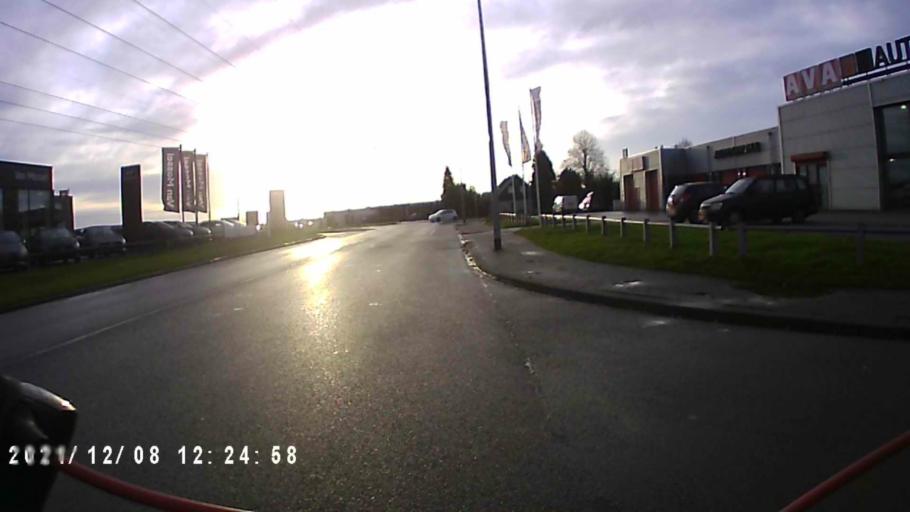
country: NL
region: Groningen
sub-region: Gemeente Groningen
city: Oosterpark
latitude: 53.2199
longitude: 6.6112
